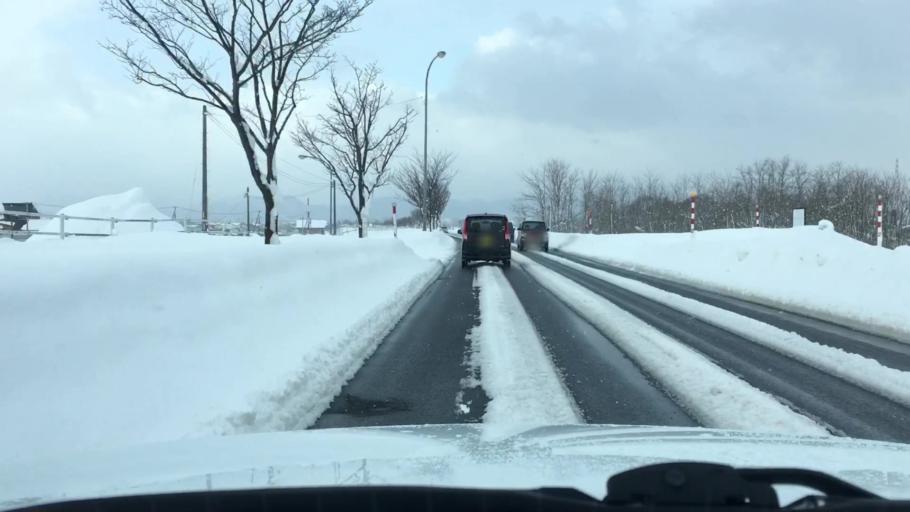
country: JP
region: Aomori
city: Hirosaki
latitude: 40.6354
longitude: 140.4719
